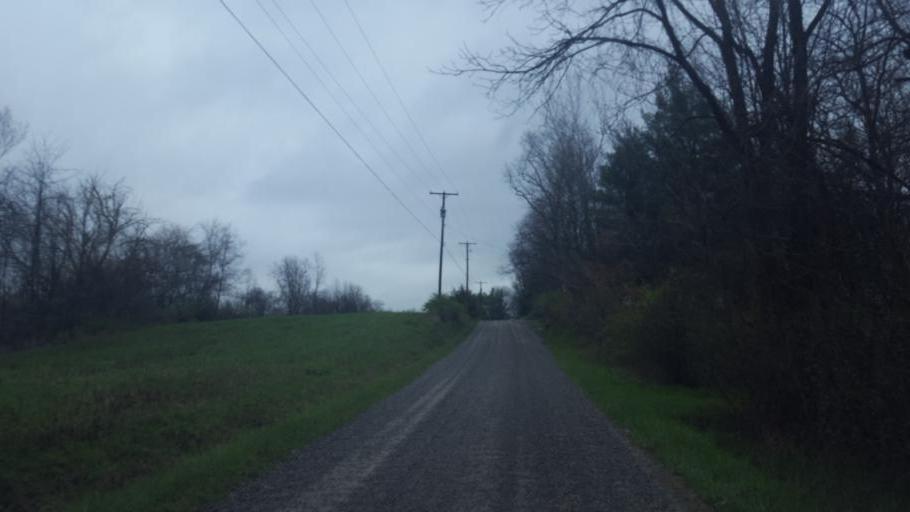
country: US
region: Ohio
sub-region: Morrow County
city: Cardington
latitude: 40.4964
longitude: -82.8727
